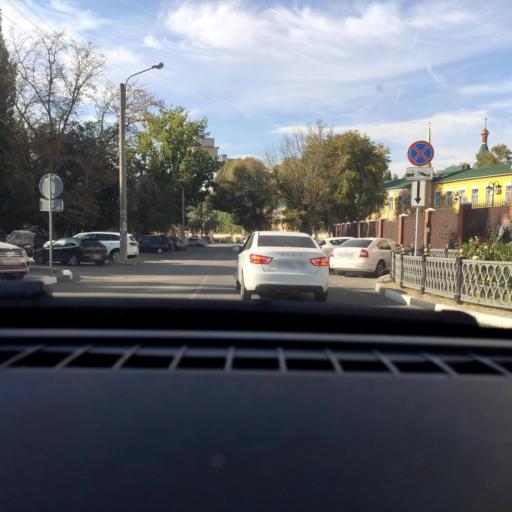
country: RU
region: Voronezj
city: Voronezh
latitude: 51.6743
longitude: 39.2490
